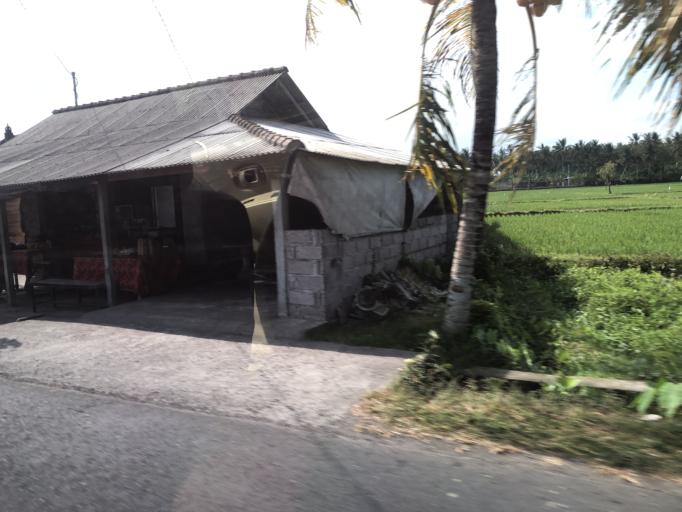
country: ID
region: Bali
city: Banjar Bucu
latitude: -8.5762
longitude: 115.1985
